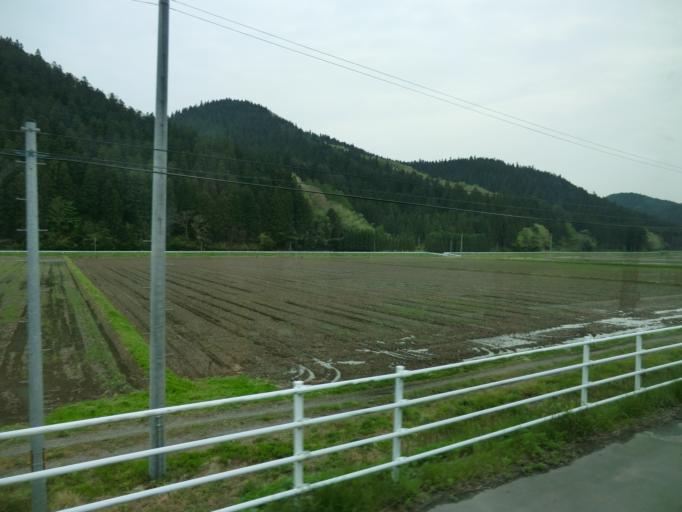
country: JP
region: Miyagi
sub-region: Oshika Gun
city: Onagawa Cho
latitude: 38.6310
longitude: 141.3514
